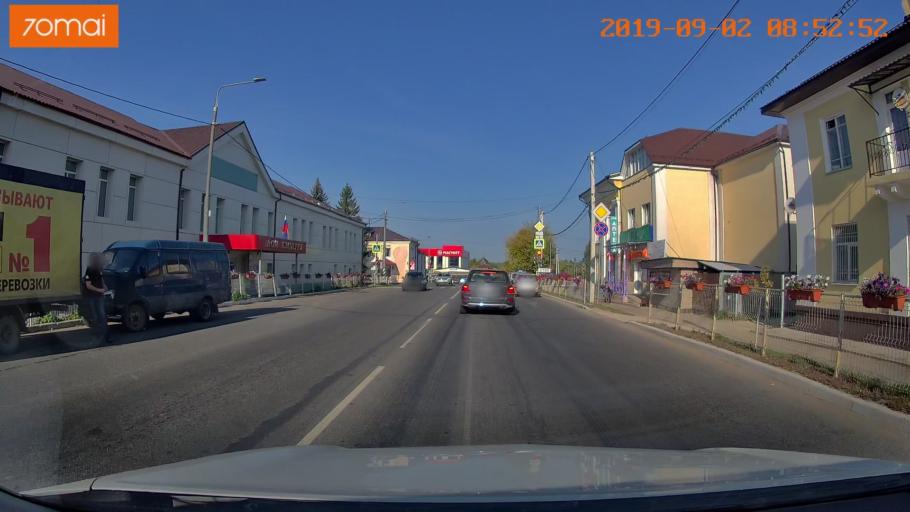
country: RU
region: Kaluga
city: Medyn'
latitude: 54.9676
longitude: 35.8582
